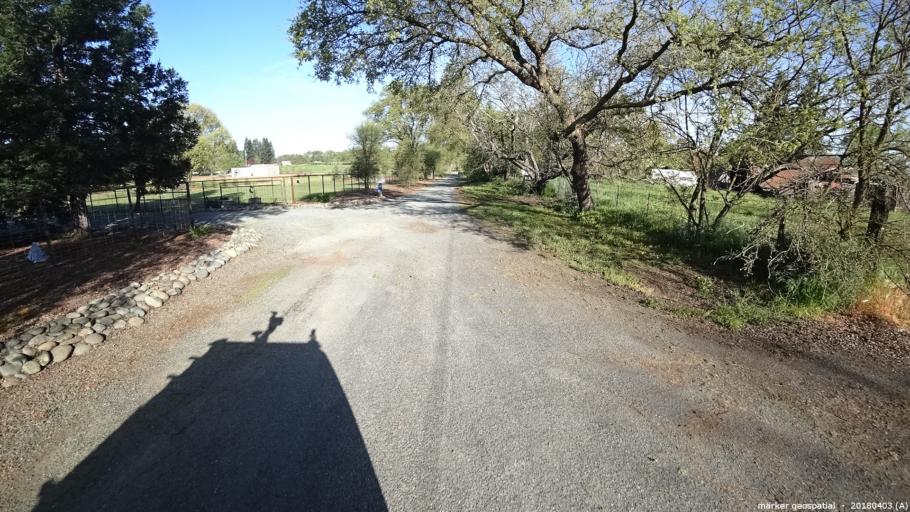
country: US
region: California
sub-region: Sacramento County
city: Wilton
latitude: 38.4383
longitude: -121.1988
